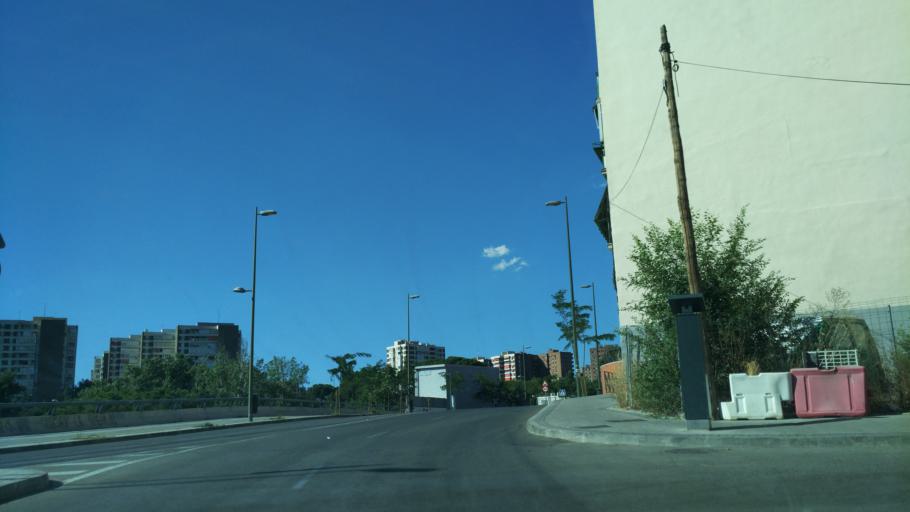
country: ES
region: Madrid
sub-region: Provincia de Madrid
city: Tetuan de las Victorias
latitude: 40.4706
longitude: -3.7023
